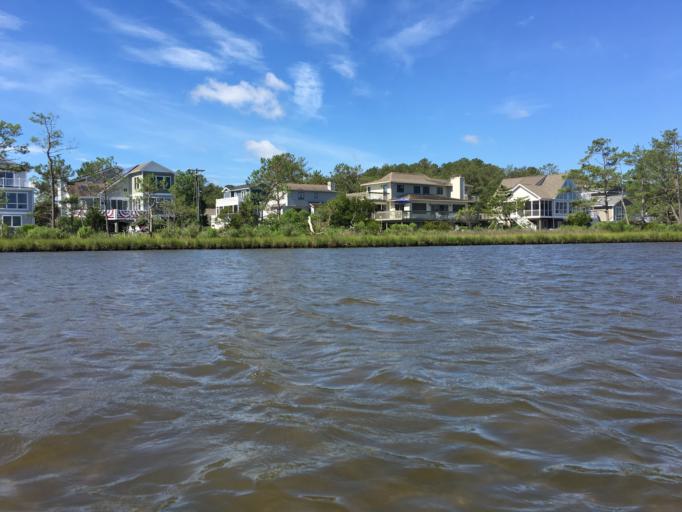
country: US
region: Delaware
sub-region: Sussex County
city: Bethany Beach
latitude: 38.5453
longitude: -75.0654
